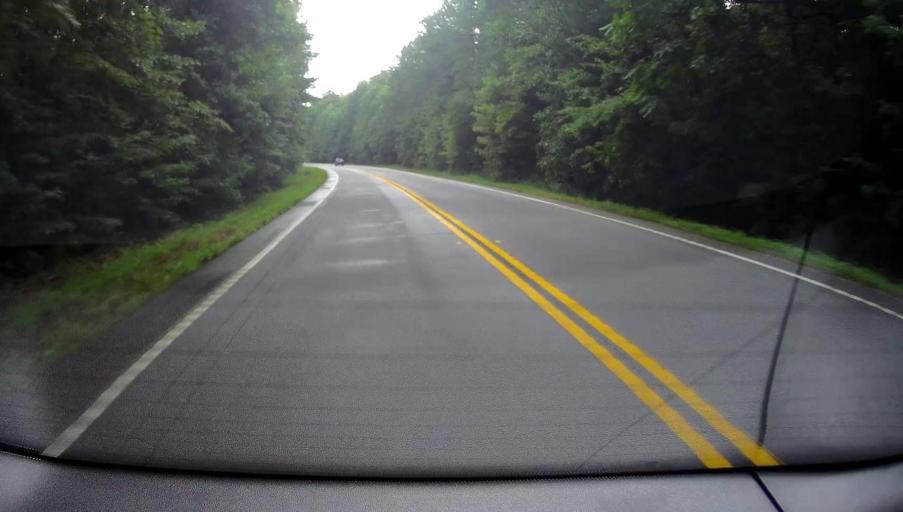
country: US
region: Georgia
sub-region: Coweta County
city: Senoia
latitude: 33.2701
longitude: -84.5548
